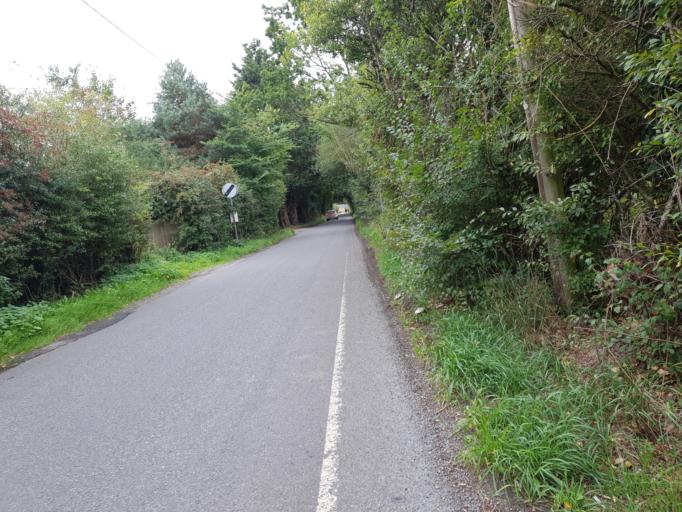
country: GB
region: England
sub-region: Suffolk
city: East Bergholt
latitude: 51.9403
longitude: 0.9951
